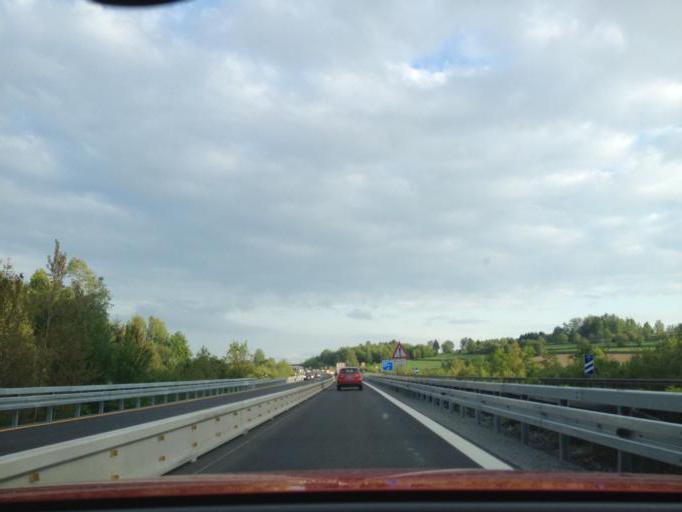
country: DE
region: Bavaria
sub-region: Upper Palatinate
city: Neustadt an der Waldnaab
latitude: 49.7425
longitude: 12.1536
